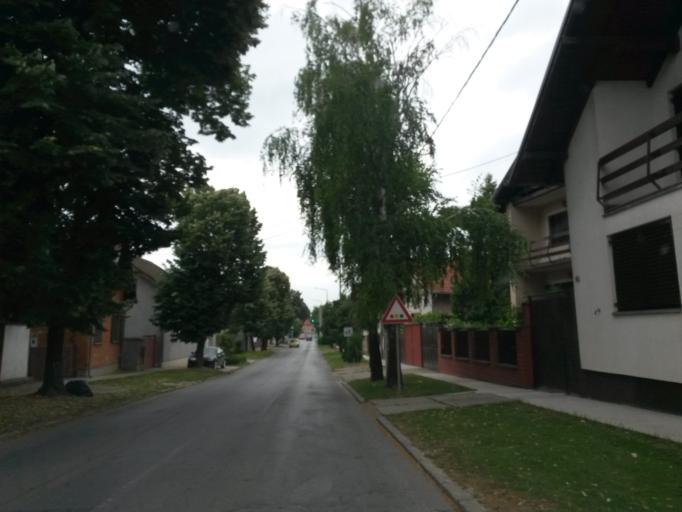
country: HR
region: Vukovarsko-Srijemska
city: Vukovar
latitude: 45.3463
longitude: 18.9928
